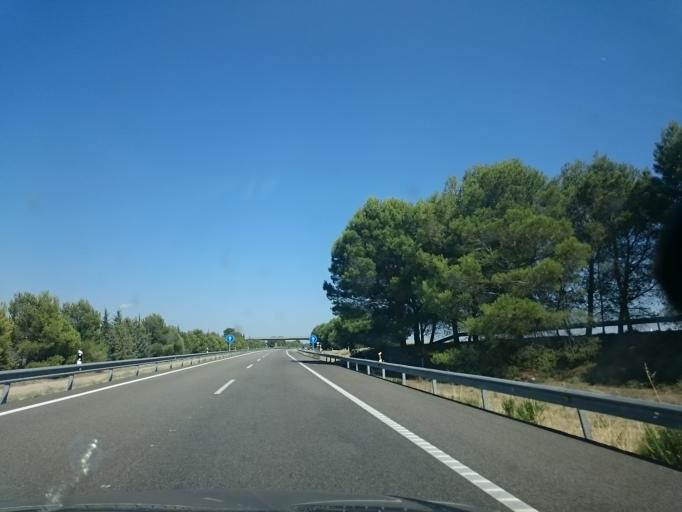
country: ES
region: Aragon
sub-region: Provincia de Zaragoza
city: Bujaraloz
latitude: 41.5245
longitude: -0.1723
